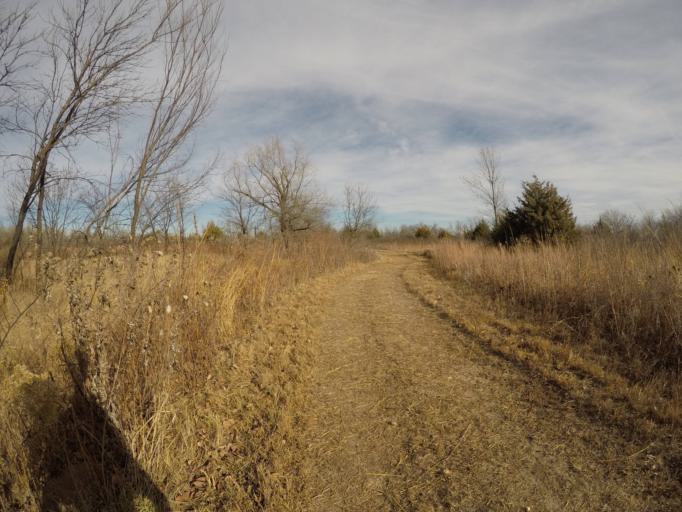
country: US
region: Kansas
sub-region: Reno County
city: Buhler
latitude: 38.1192
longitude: -97.8573
